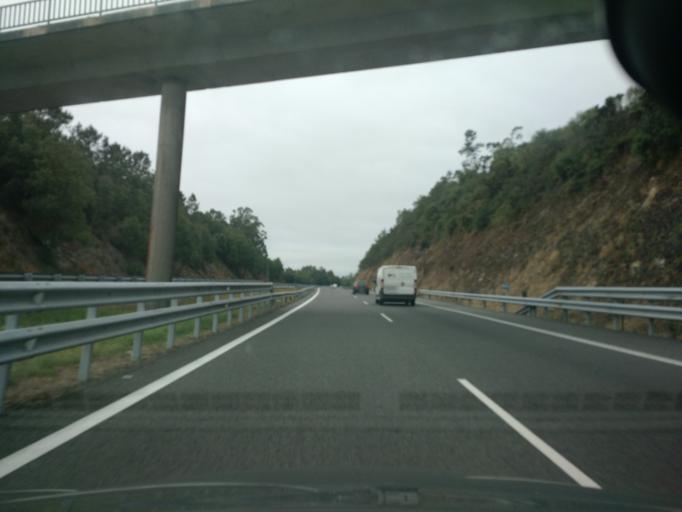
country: ES
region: Galicia
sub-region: Provincia da Coruna
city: Abegondo
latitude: 43.1597
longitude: -8.3268
